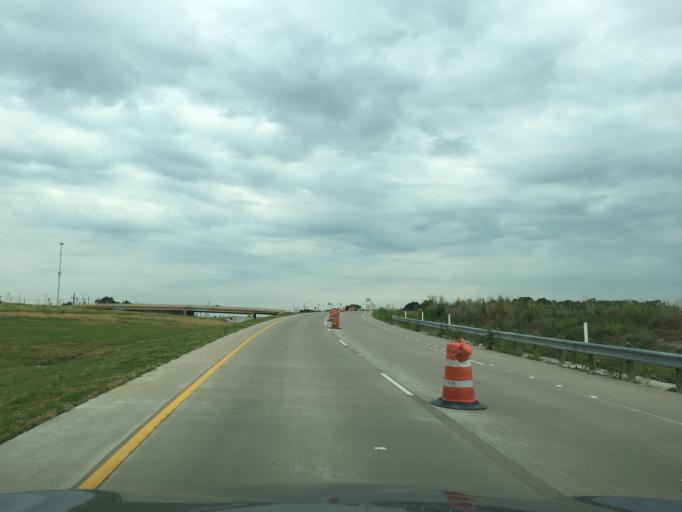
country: US
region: Texas
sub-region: Collin County
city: Melissa
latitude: 33.3064
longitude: -96.5907
